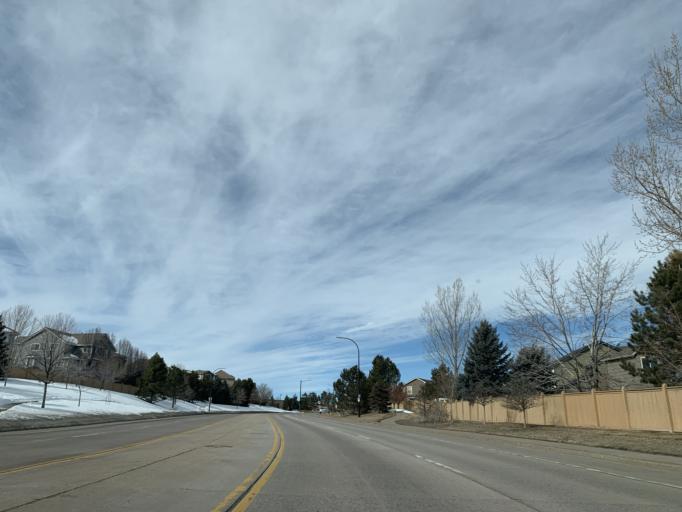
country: US
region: Colorado
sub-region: Douglas County
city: Carriage Club
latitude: 39.5255
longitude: -104.9360
